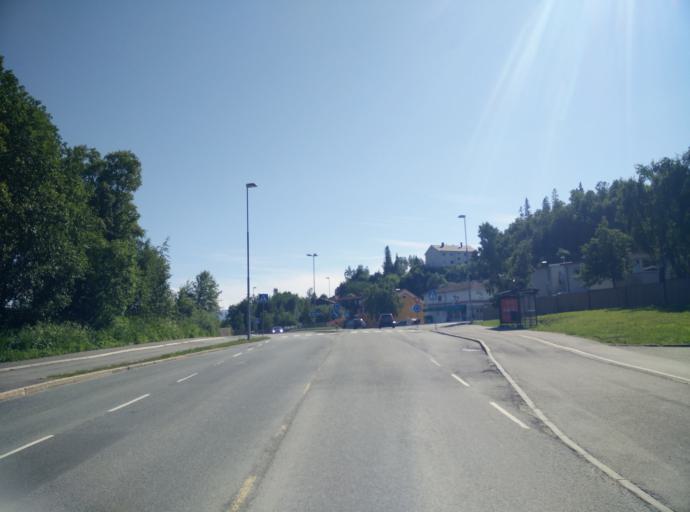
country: NO
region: Sor-Trondelag
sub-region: Trondheim
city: Trondheim
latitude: 63.4021
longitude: 10.3576
